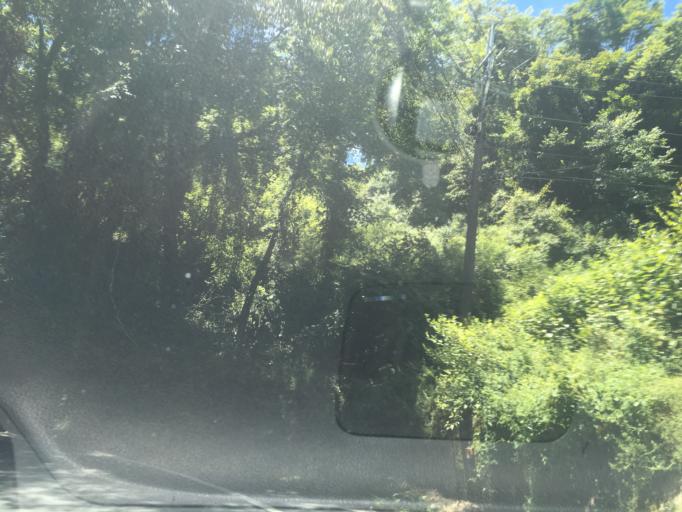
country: TW
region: Taiwan
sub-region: Nantou
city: Puli
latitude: 24.2509
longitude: 121.2519
